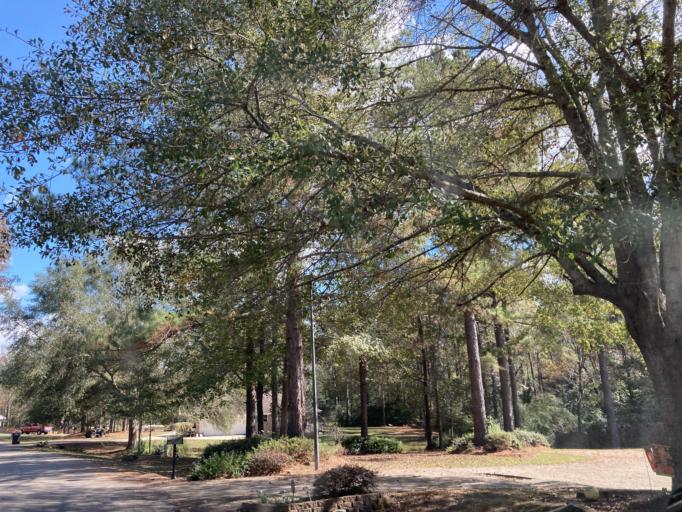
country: US
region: Mississippi
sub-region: Lamar County
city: Sumrall
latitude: 31.3633
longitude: -89.5179
